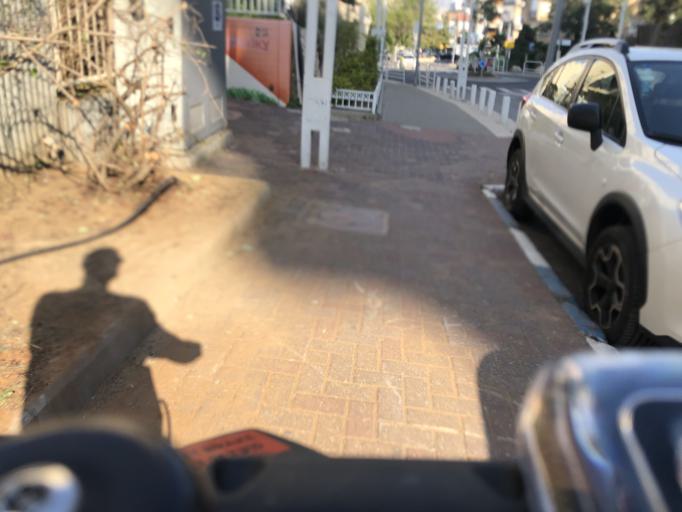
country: IL
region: Tel Aviv
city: Giv`atayim
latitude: 32.0680
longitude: 34.8124
